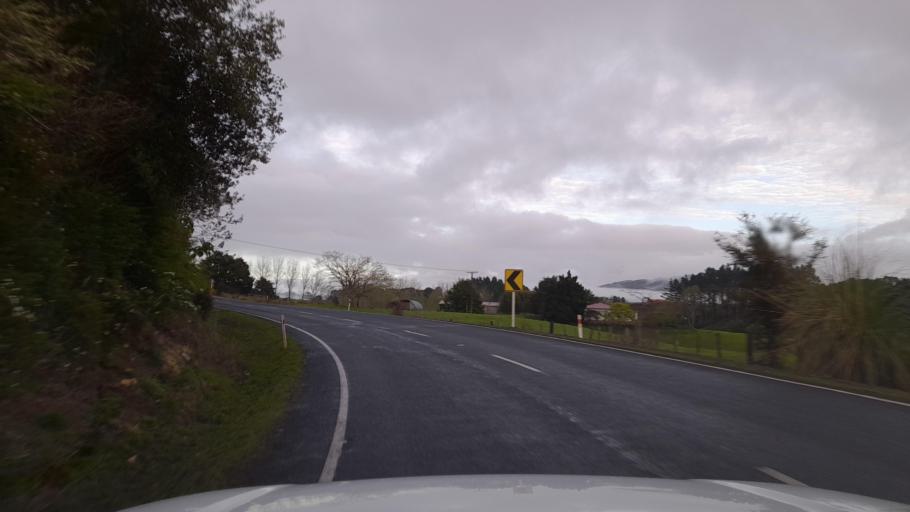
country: NZ
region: Northland
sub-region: Whangarei
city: Maungatapere
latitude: -35.7048
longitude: 174.0144
